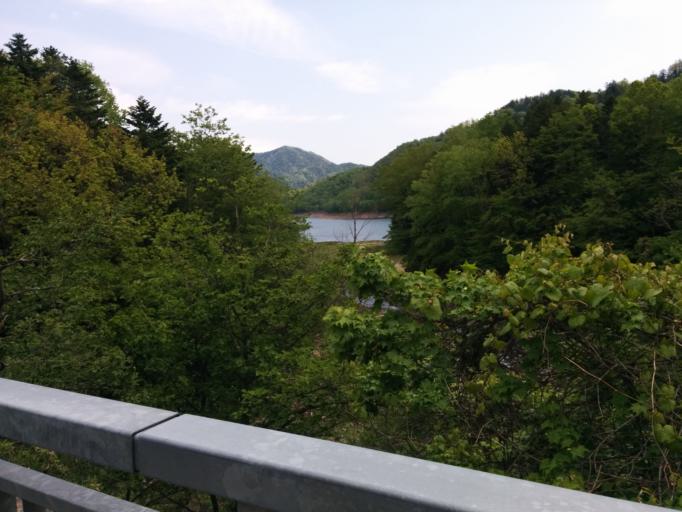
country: JP
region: Hokkaido
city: Otofuke
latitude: 43.3680
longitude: 143.1939
